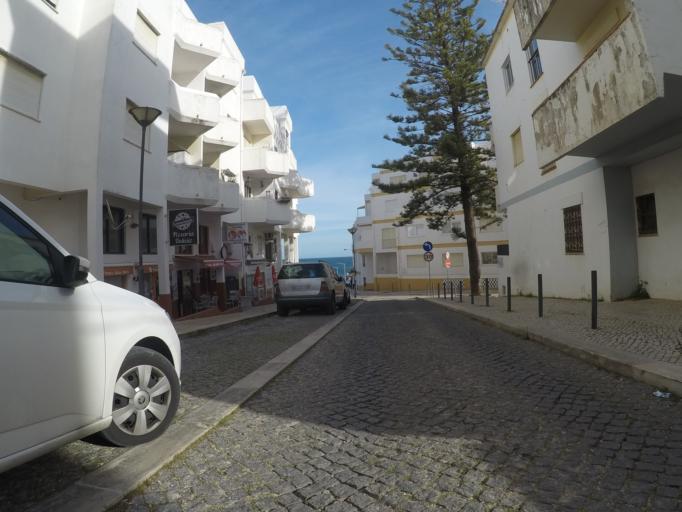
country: PT
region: Faro
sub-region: Lagos
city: Lagos
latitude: 37.0863
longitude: -8.7309
